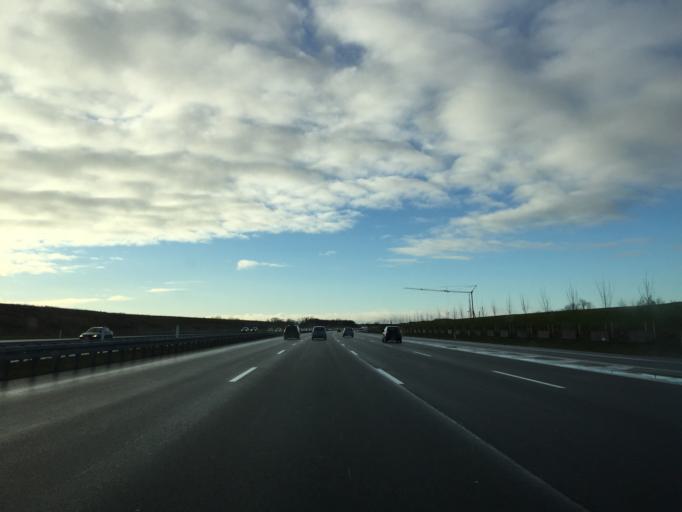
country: DK
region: Zealand
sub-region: Greve Kommune
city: Greve
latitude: 55.5802
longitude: 12.2567
